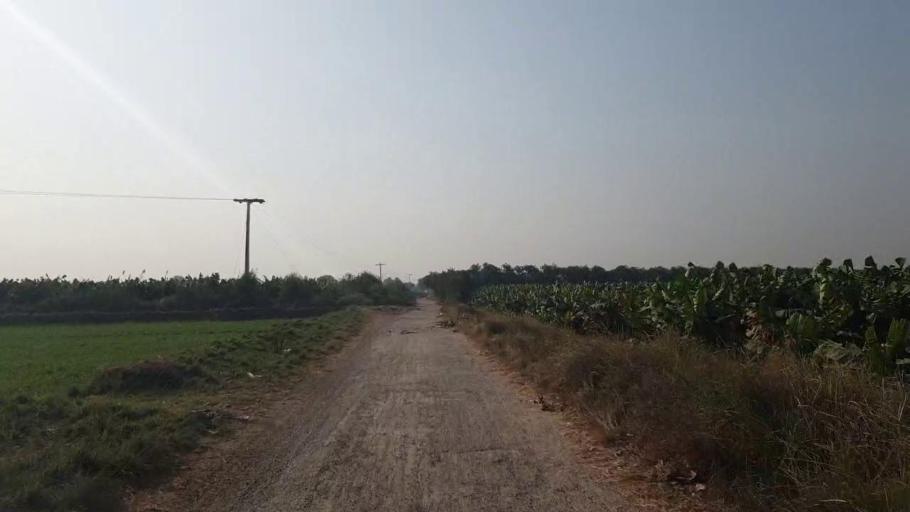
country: PK
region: Sindh
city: Kotri
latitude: 25.3436
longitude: 68.3228
